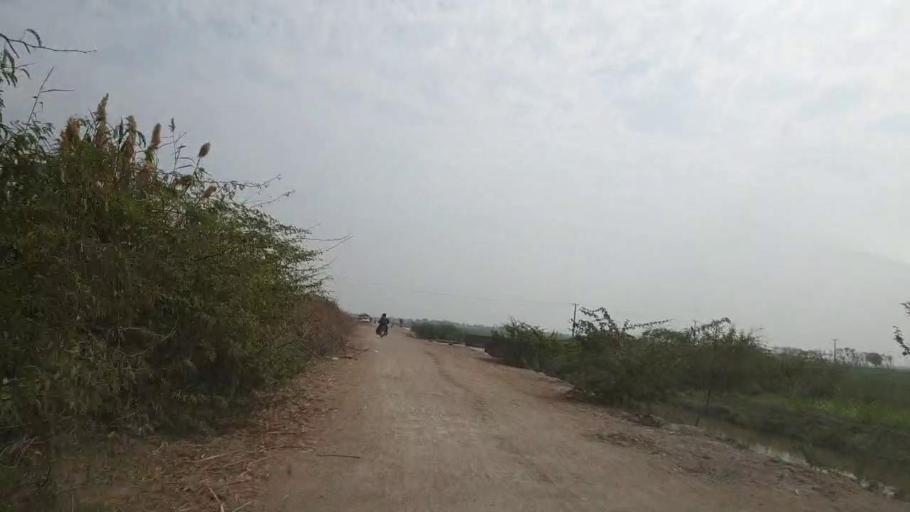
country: PK
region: Sindh
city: Mirpur Khas
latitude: 25.5366
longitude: 69.1302
